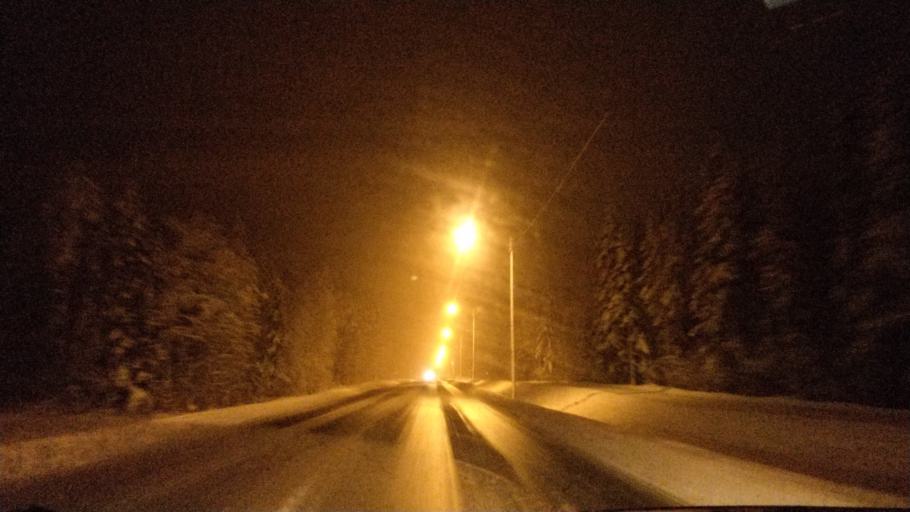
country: FI
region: Lapland
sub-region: Rovaniemi
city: Rovaniemi
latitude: 66.4236
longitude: 25.4210
